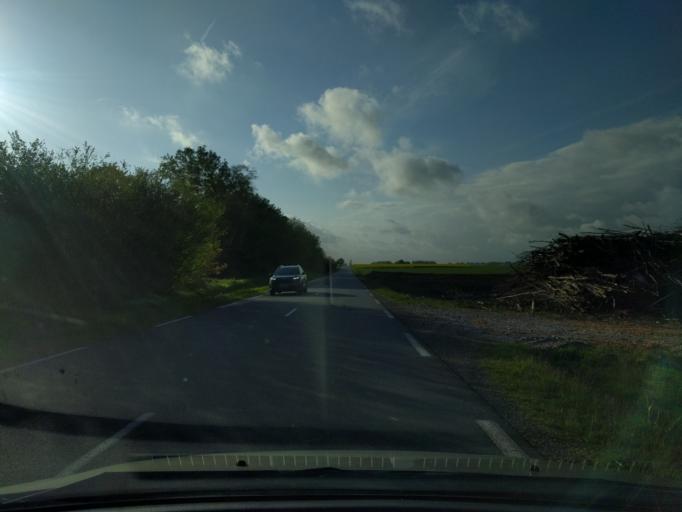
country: FR
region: Haute-Normandie
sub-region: Departement de l'Eure
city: Conches-en-Ouche
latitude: 48.9254
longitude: 0.9965
